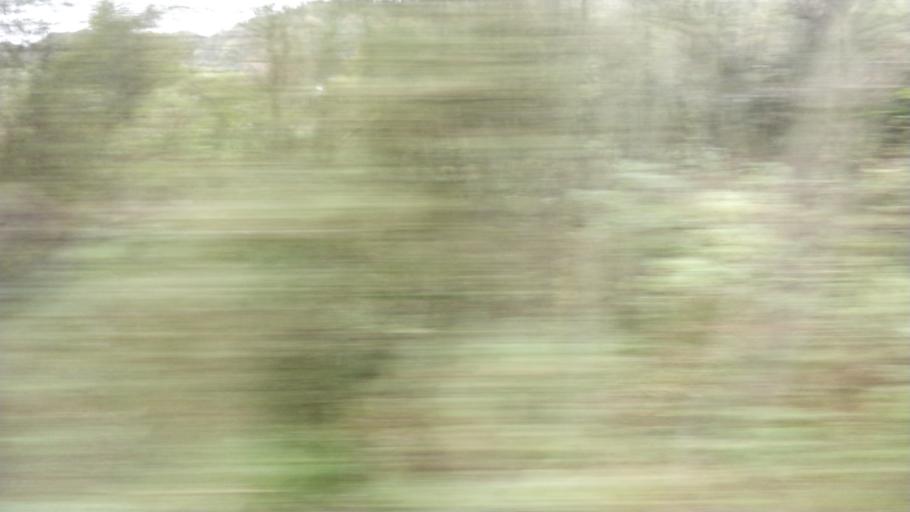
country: GB
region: England
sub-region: Lancashire
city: Parbold
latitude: 53.5853
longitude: -2.7470
